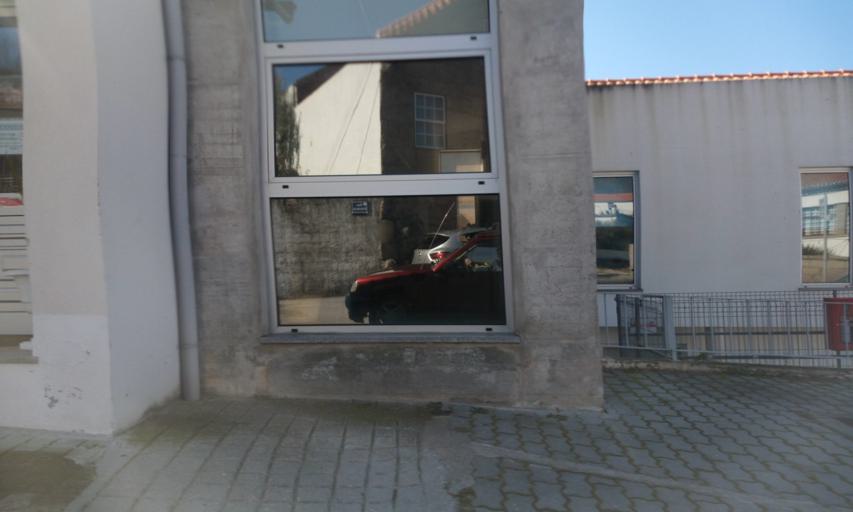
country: PT
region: Guarda
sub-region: Manteigas
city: Manteigas
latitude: 40.4683
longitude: -7.5978
